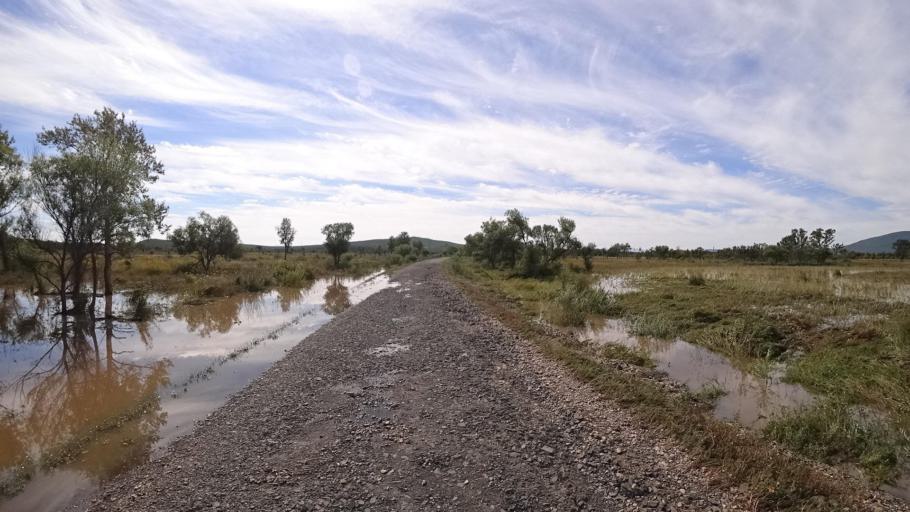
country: RU
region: Primorskiy
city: Kirovskiy
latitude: 44.7750
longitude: 133.6259
